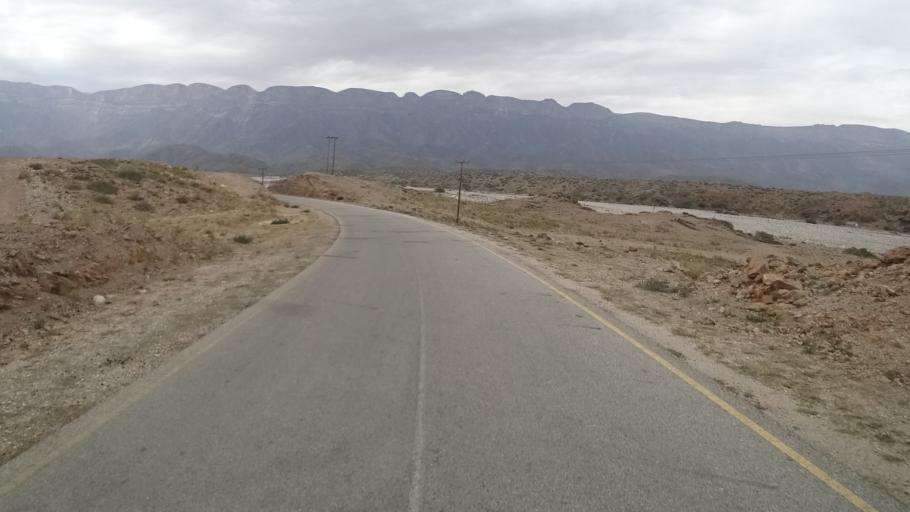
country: OM
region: Zufar
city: Salalah
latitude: 17.1577
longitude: 54.9964
